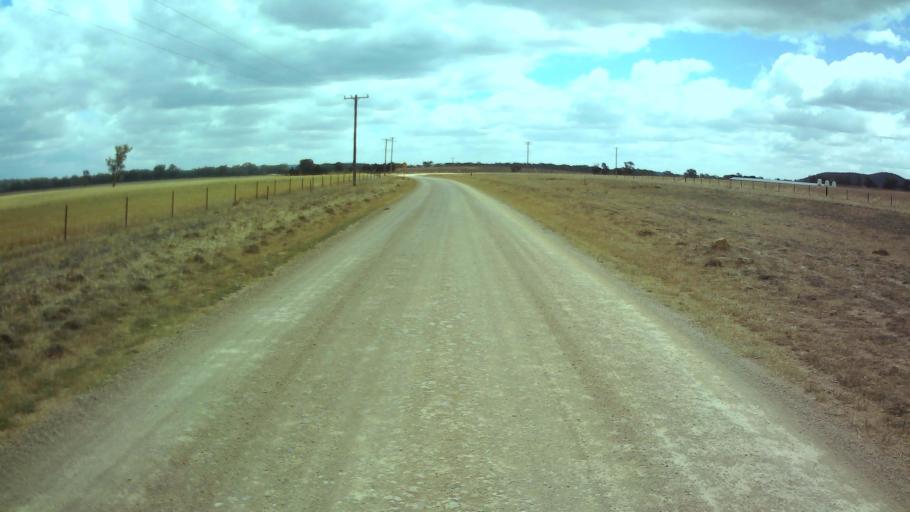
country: AU
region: New South Wales
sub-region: Weddin
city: Grenfell
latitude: -33.9391
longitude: 148.2877
